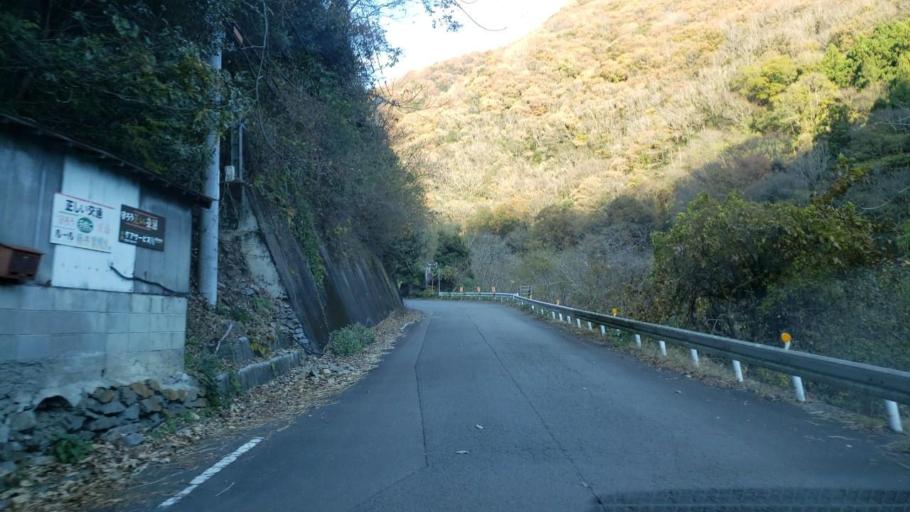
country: JP
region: Tokushima
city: Wakimachi
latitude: 34.0825
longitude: 134.0723
